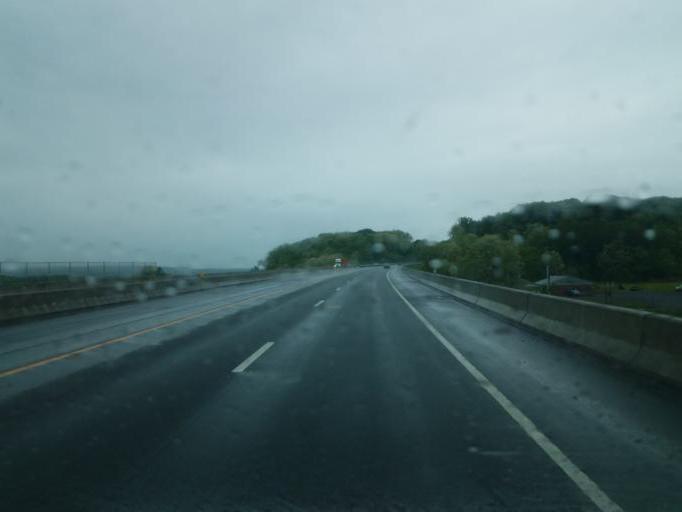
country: US
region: New York
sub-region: Herkimer County
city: Mohawk
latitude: 43.0176
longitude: -75.0079
